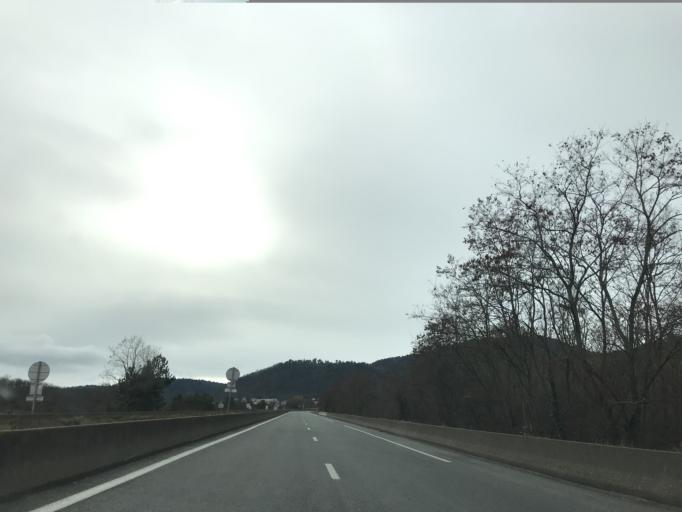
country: FR
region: Auvergne
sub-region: Departement du Puy-de-Dome
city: Beaumont
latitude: 45.7417
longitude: 3.0746
